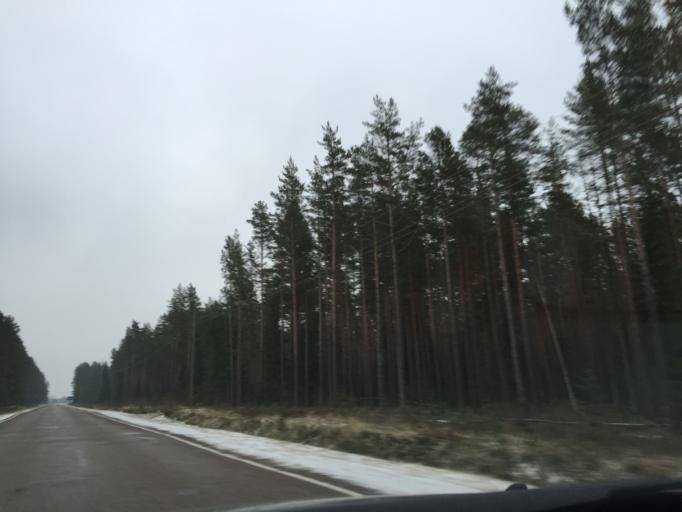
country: LV
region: Saulkrastu
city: Saulkrasti
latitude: 57.4927
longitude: 24.4221
